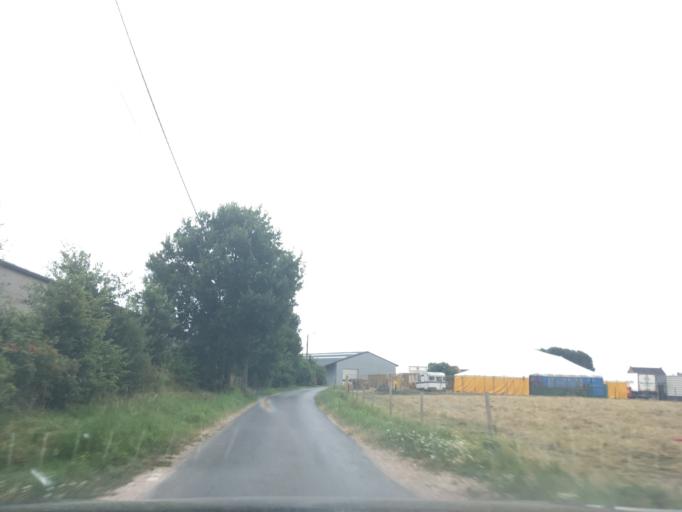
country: BE
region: Flanders
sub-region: Provincie West-Vlaanderen
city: Ardooie
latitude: 50.9657
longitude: 3.1934
